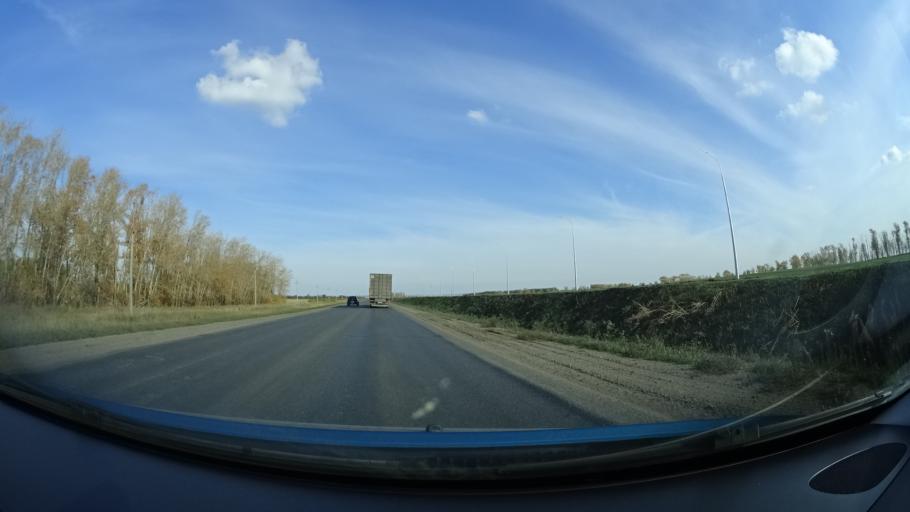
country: RU
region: Bashkortostan
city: Buzdyak
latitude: 54.6398
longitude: 54.4937
